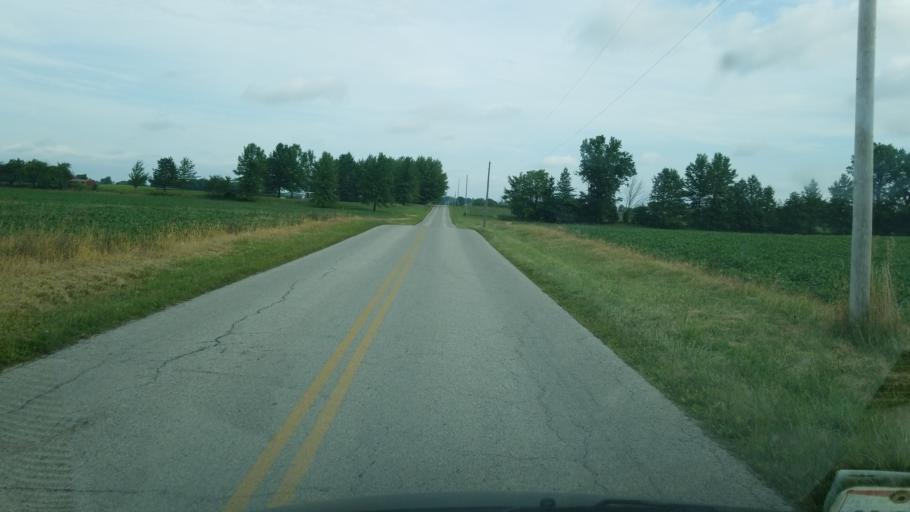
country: US
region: Ohio
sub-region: Seneca County
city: Tiffin
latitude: 41.1011
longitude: -83.0930
